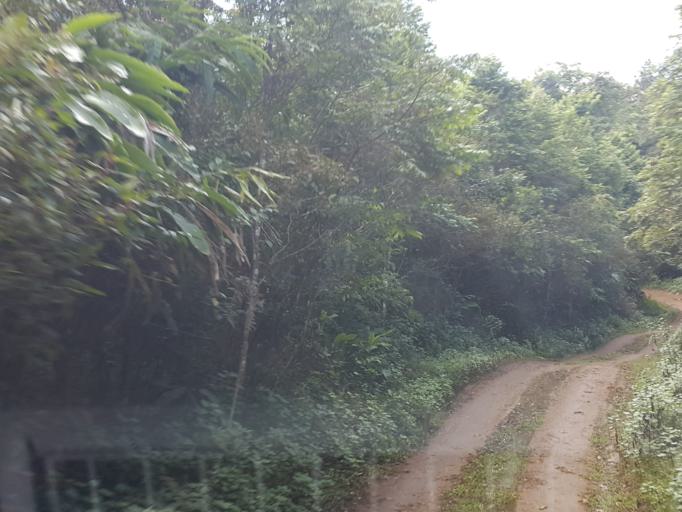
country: TH
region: Chiang Mai
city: Wiang Haeng
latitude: 19.5551
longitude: 98.8097
